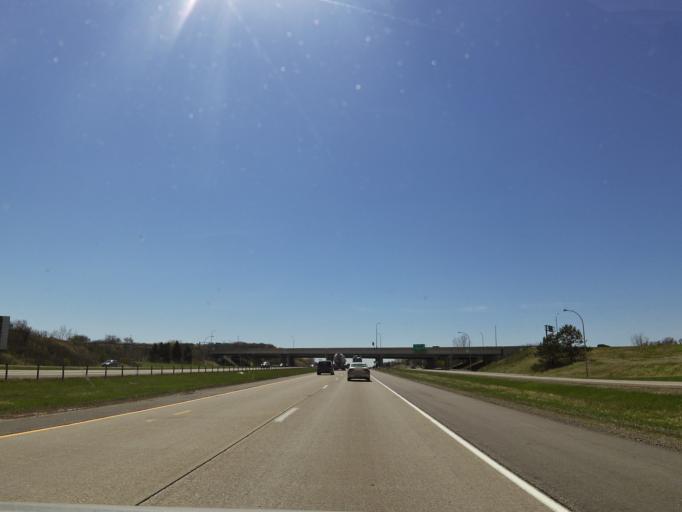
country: US
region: Minnesota
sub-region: Dakota County
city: Apple Valley
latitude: 44.7802
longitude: -93.2146
